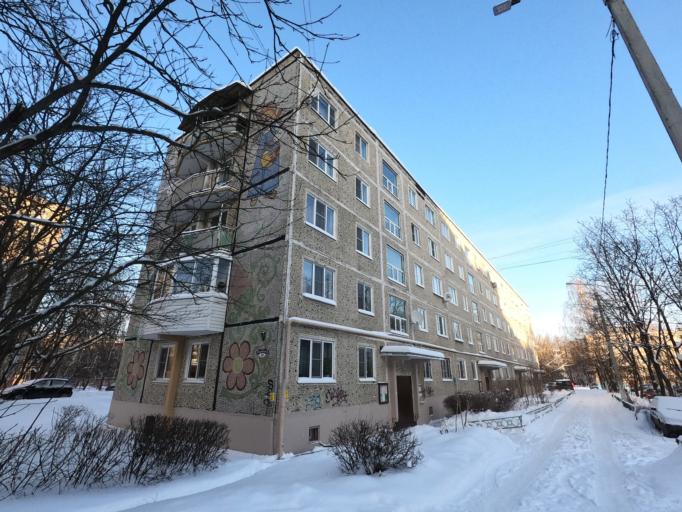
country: RU
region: Moskovskaya
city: Dmitrov
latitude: 56.3469
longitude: 37.5247
